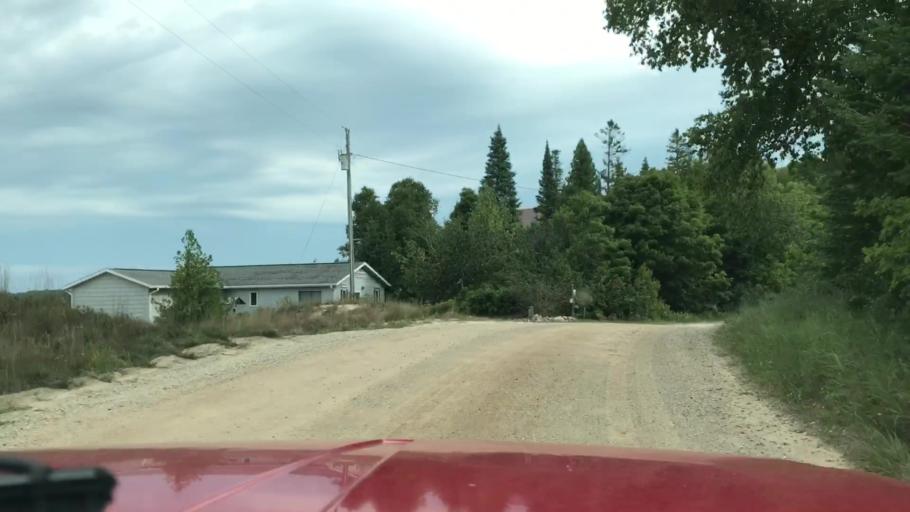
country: US
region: Michigan
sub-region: Charlevoix County
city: Charlevoix
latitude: 45.7325
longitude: -85.5626
